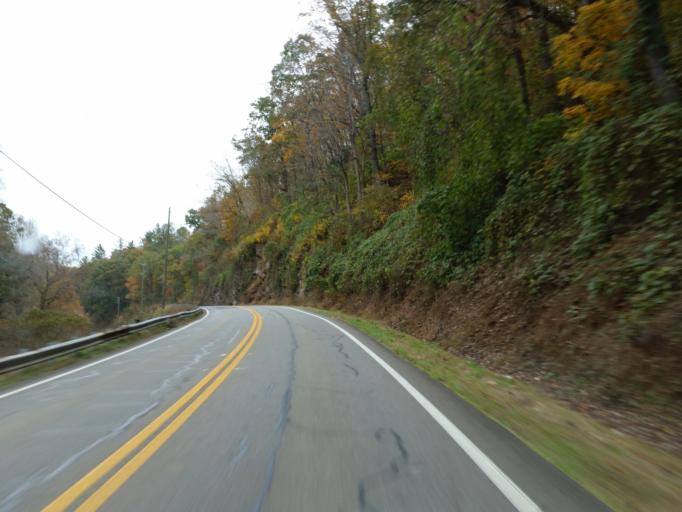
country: US
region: Georgia
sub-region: Pickens County
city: Jasper
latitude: 34.5133
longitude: -84.4386
